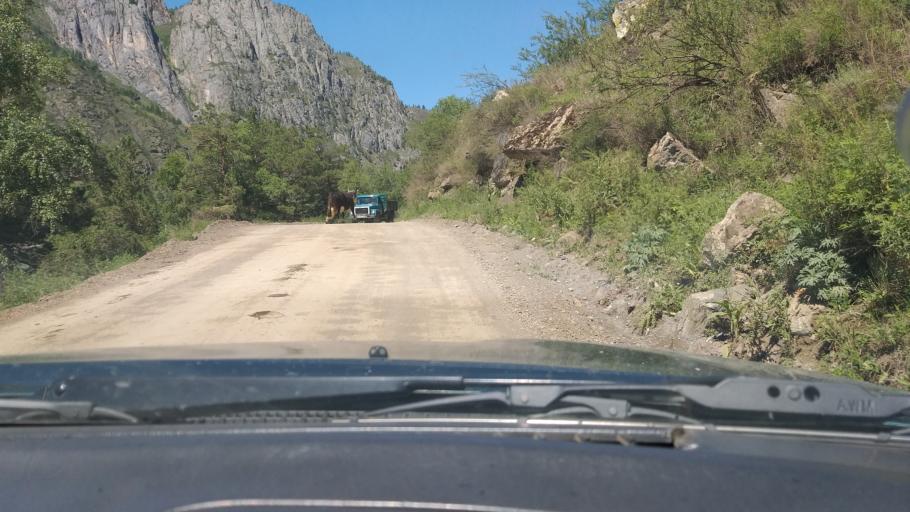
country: RU
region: Altay
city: Chemal
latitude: 51.2030
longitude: 86.0854
